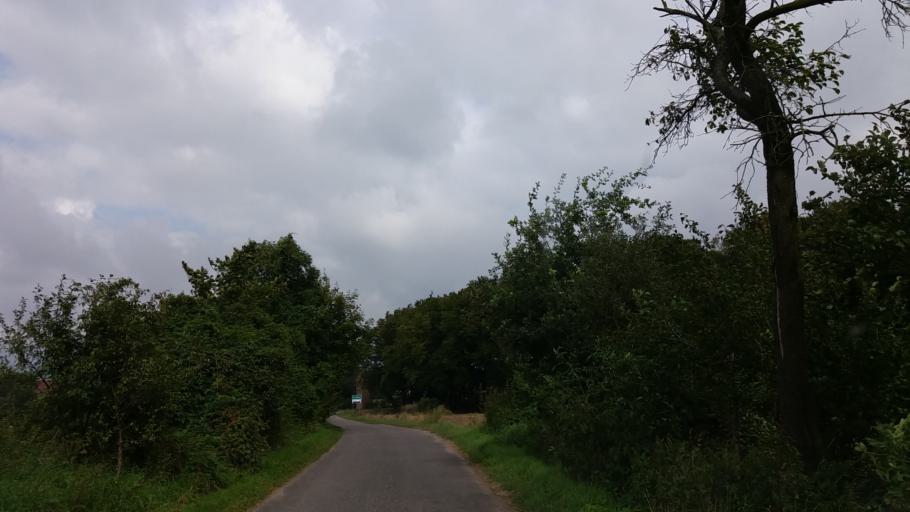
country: PL
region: West Pomeranian Voivodeship
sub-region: Powiat choszczenski
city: Krzecin
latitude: 53.1115
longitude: 15.4935
